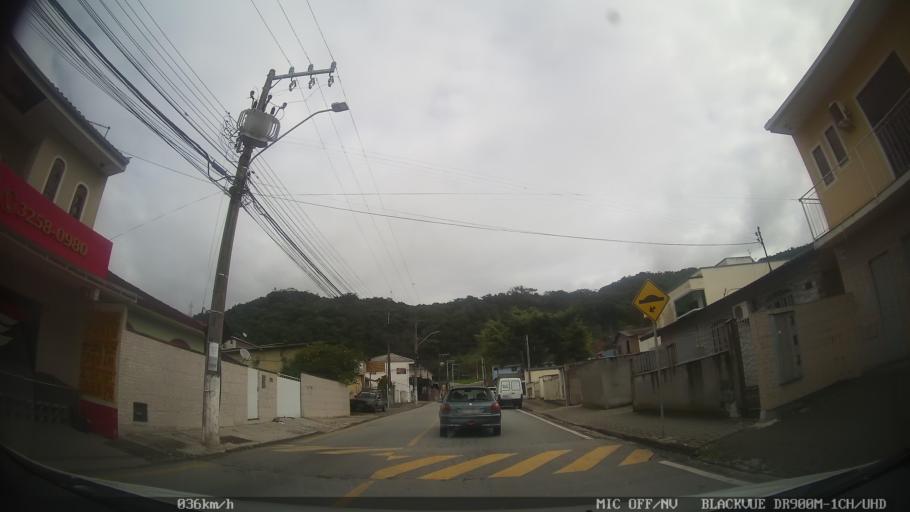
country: BR
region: Santa Catarina
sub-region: Biguacu
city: Biguacu
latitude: -27.5476
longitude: -48.6451
